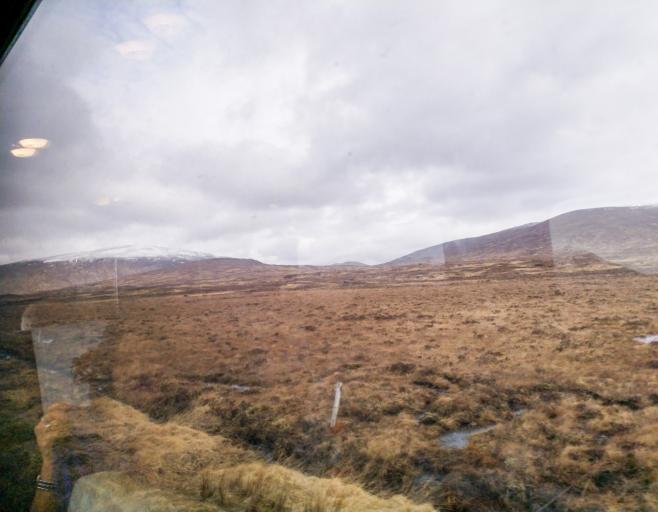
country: GB
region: Scotland
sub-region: Highland
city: Spean Bridge
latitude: 56.7328
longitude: -4.6523
